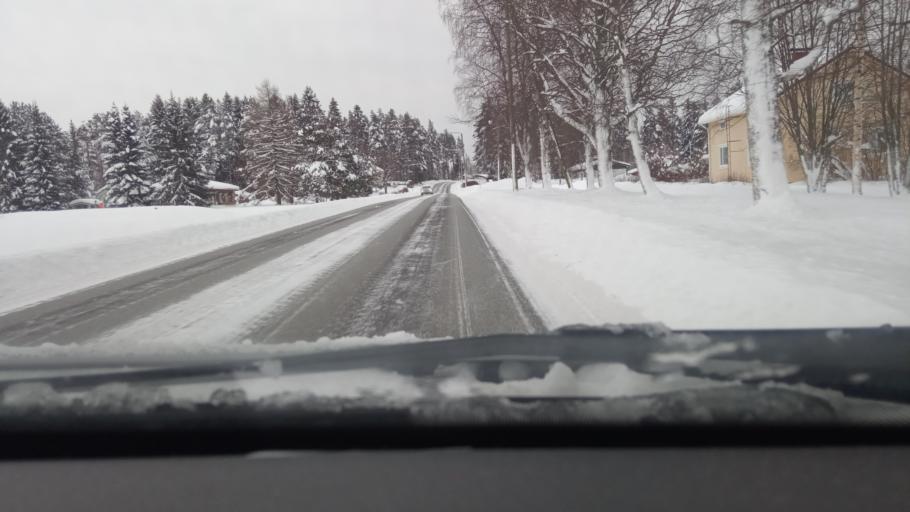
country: FI
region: Southern Ostrobothnia
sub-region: Jaerviseutu
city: Alajaervi
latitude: 62.9897
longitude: 23.8458
